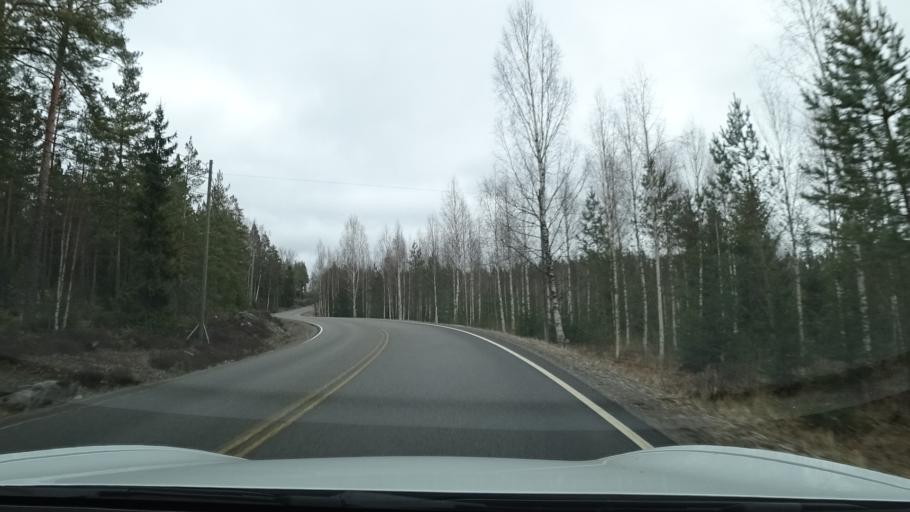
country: FI
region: Uusimaa
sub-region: Porvoo
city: Askola
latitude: 60.5730
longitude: 25.5838
